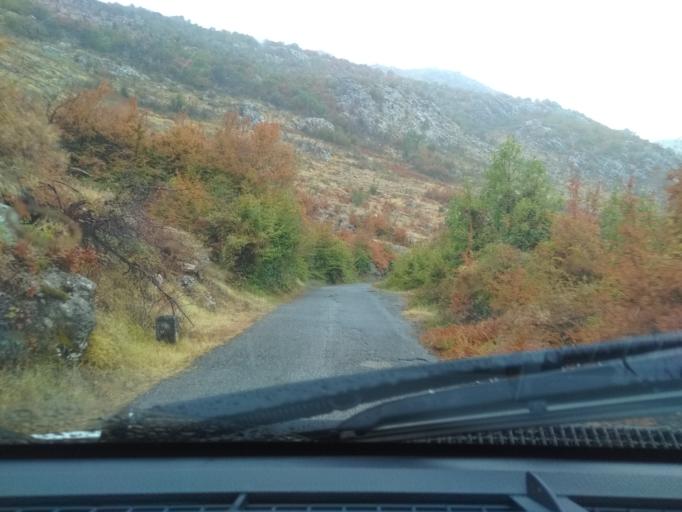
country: ME
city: Stari Bar
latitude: 42.1672
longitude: 19.1980
